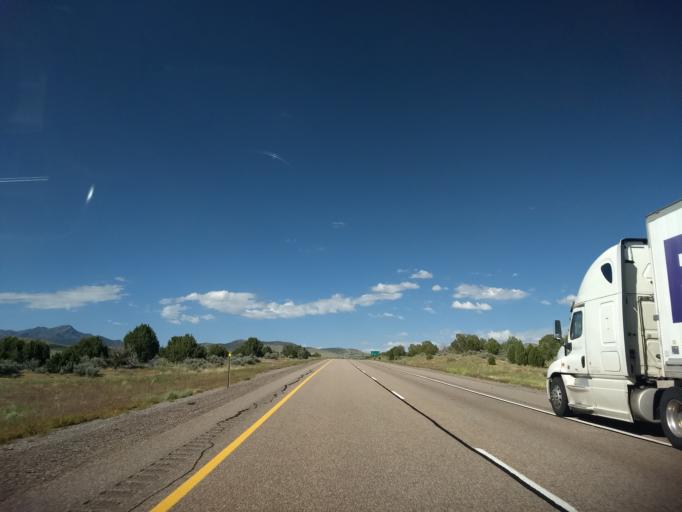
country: US
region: Utah
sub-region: Millard County
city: Fillmore
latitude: 39.1556
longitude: -112.2275
